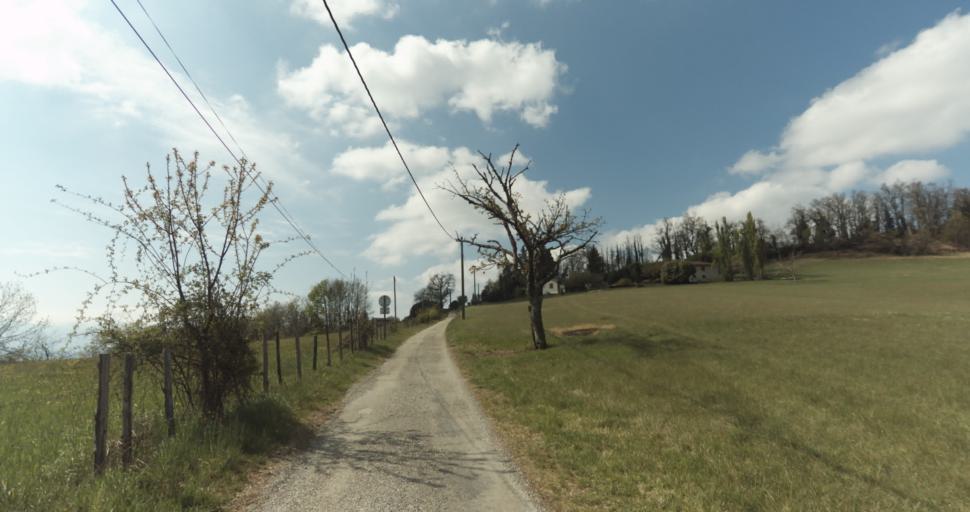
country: FR
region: Rhone-Alpes
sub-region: Departement de l'Isere
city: Saint-Marcellin
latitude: 45.1626
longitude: 5.3110
